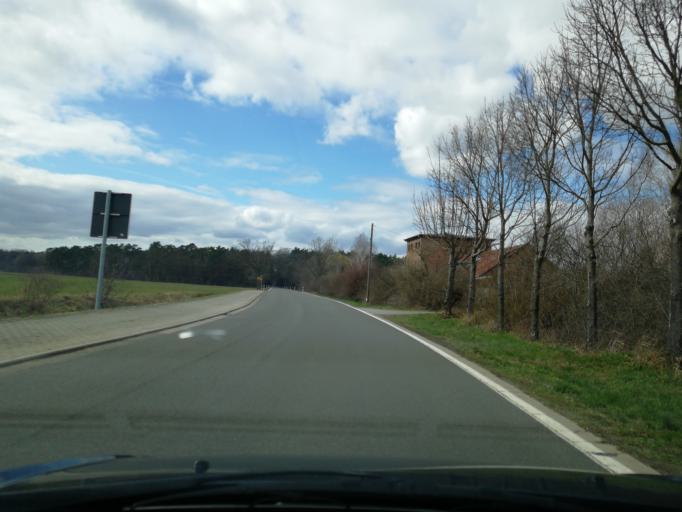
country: DE
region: Brandenburg
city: Altdobern
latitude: 51.7148
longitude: 14.0372
